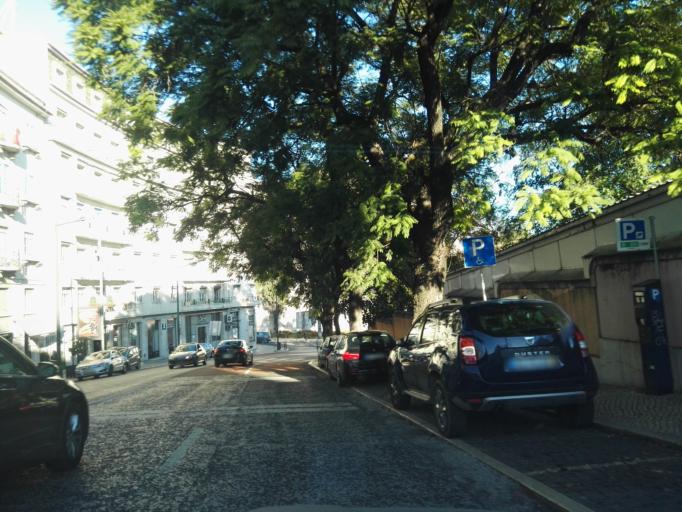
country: PT
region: Lisbon
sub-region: Lisbon
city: Lisbon
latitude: 38.7207
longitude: -9.1567
